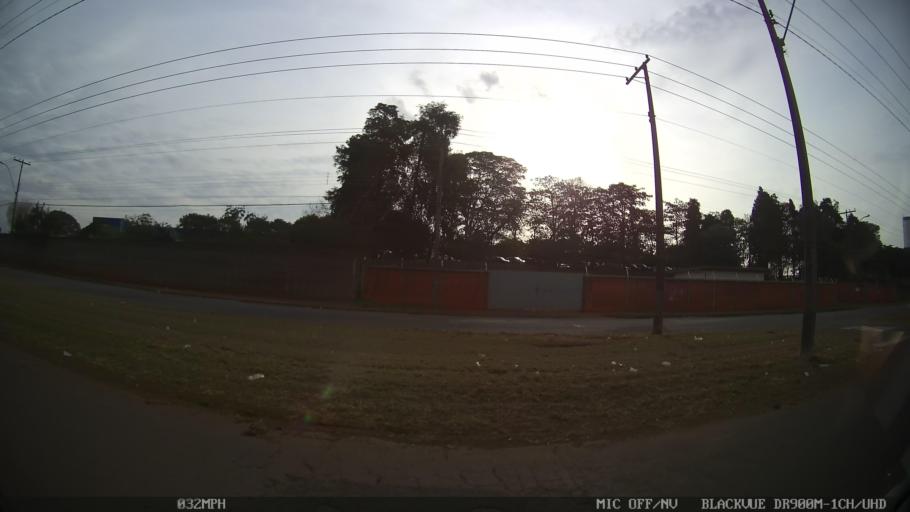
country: BR
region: Sao Paulo
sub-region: Piracicaba
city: Piracicaba
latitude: -22.7306
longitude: -47.5871
